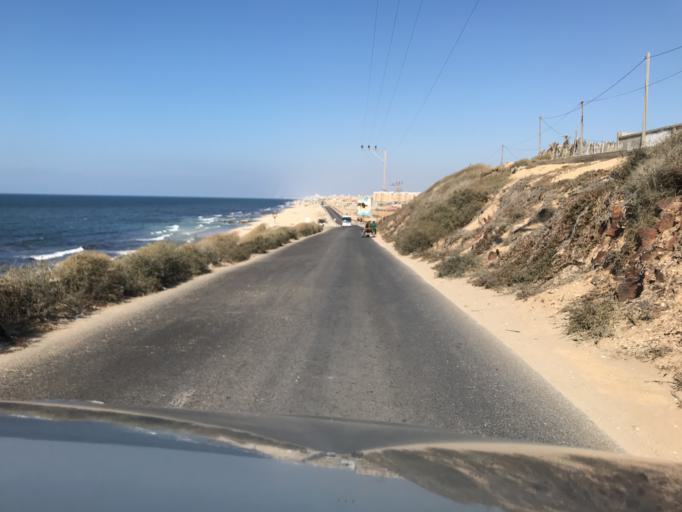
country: PS
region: Gaza Strip
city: Az Zuwaydah
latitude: 31.4602
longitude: 34.3724
